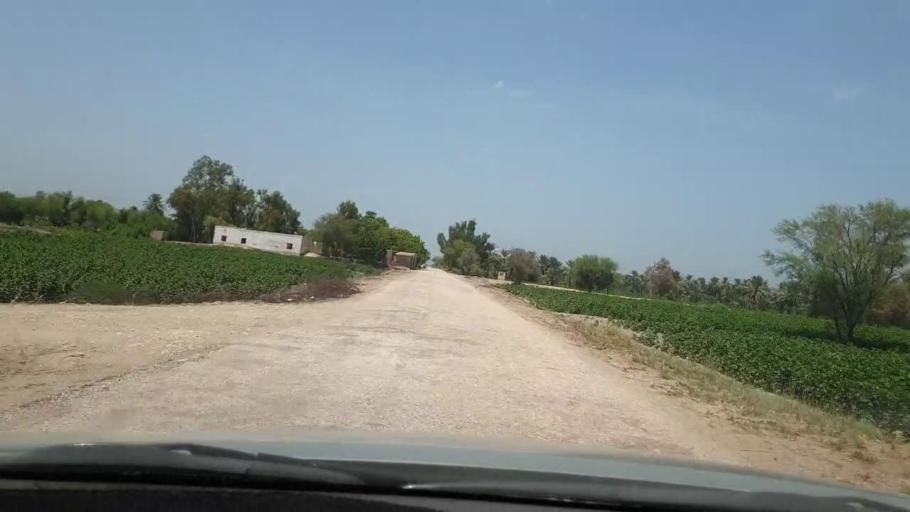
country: PK
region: Sindh
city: Pano Aqil
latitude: 27.7074
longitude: 69.2169
